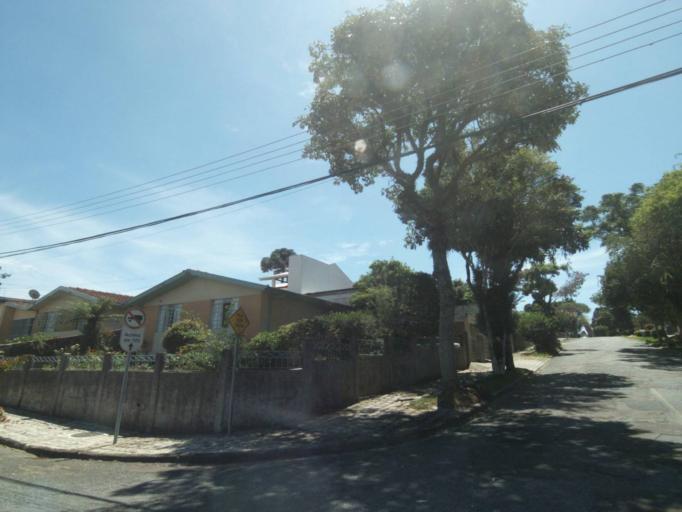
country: BR
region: Parana
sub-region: Pinhais
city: Pinhais
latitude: -25.4670
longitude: -49.2384
